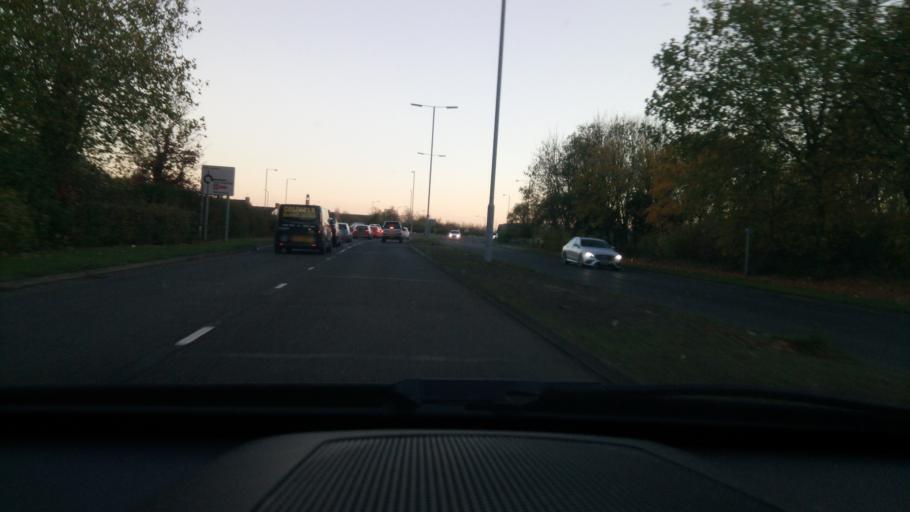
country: GB
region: England
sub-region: Peterborough
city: Peterborough
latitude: 52.5850
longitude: -0.2540
